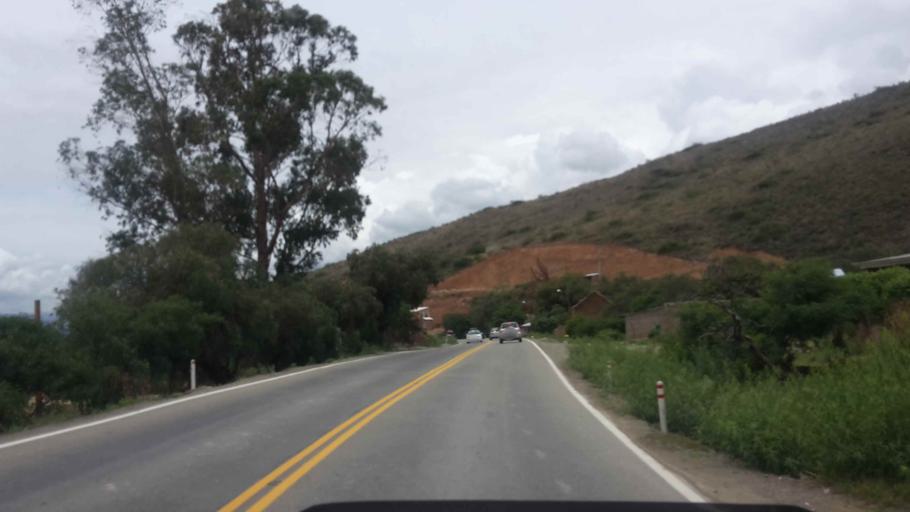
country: BO
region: Cochabamba
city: Punata
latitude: -17.5141
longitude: -65.8140
